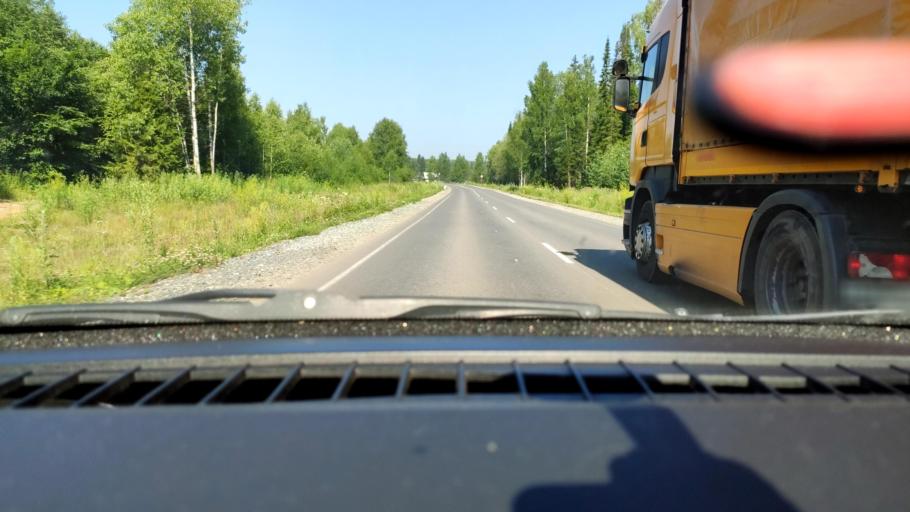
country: RU
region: Perm
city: Nytva
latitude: 57.9317
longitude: 55.4831
